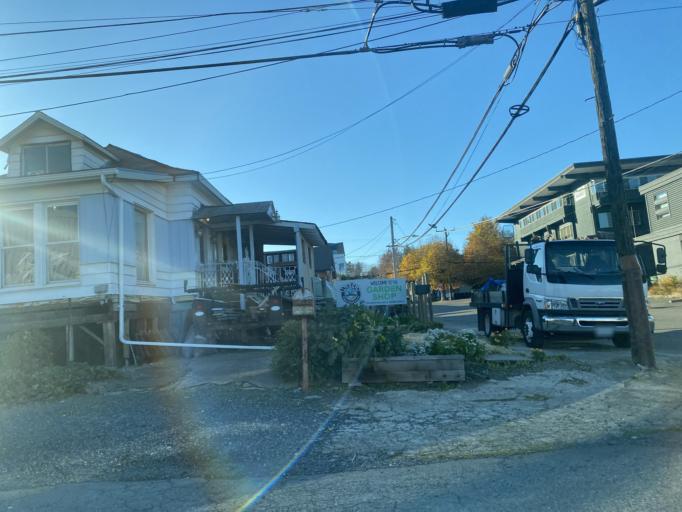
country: US
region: Washington
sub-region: King County
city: Seattle
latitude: 47.6574
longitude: -122.3847
